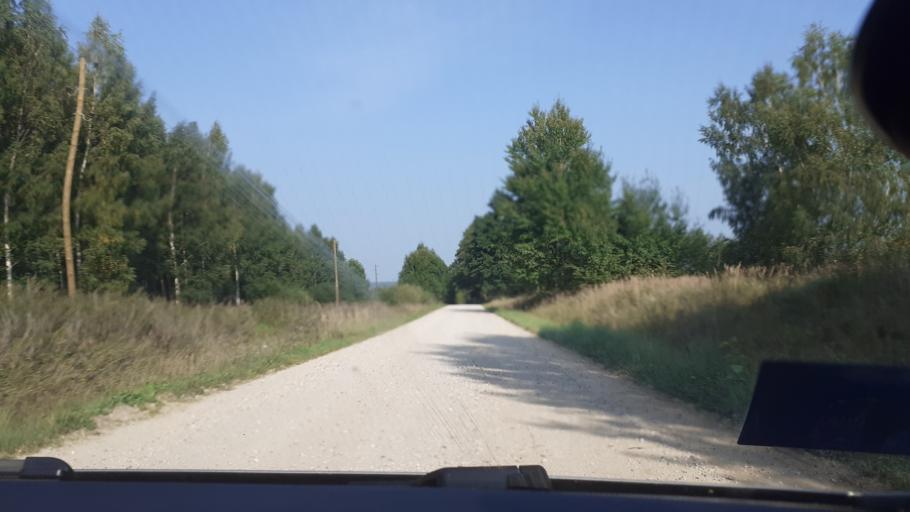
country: LV
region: Kuldigas Rajons
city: Kuldiga
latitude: 56.9823
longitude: 21.8597
